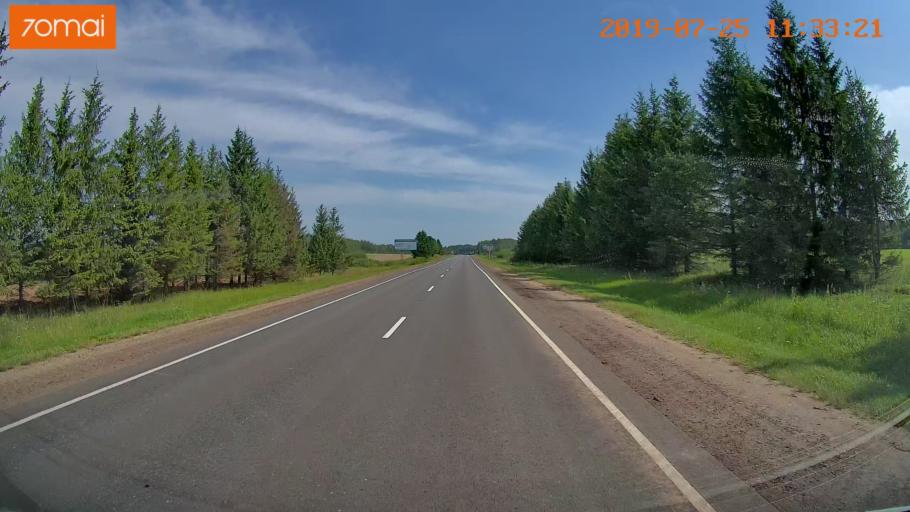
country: RU
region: Ivanovo
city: Privolzhsk
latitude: 57.3933
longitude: 41.3890
